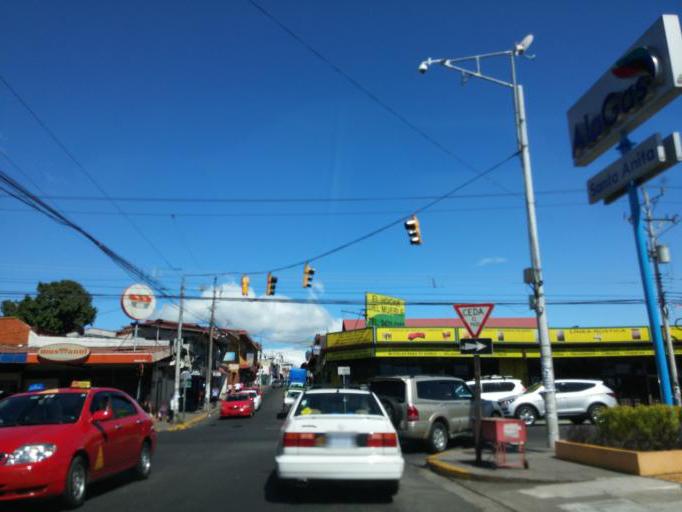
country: CR
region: Alajuela
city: Alajuela
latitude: 10.0148
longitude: -84.2186
